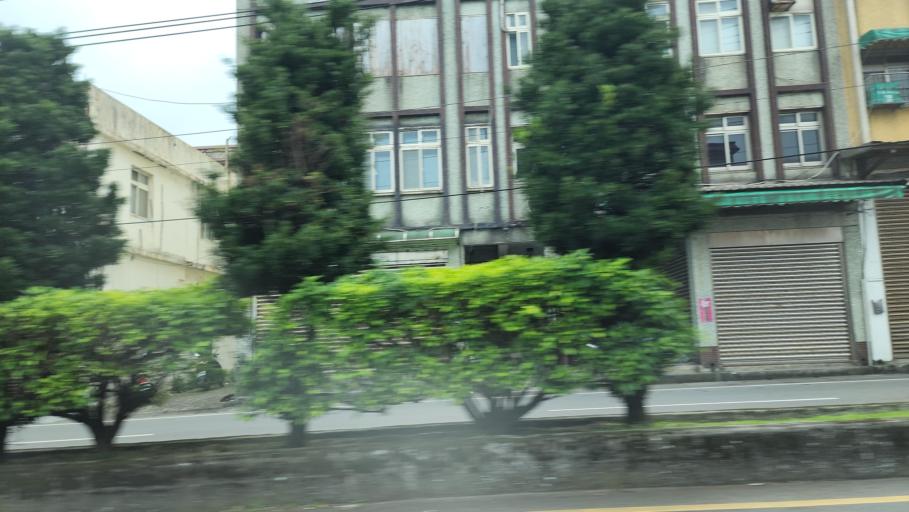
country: TW
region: Taiwan
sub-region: Keelung
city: Keelung
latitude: 25.2127
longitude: 121.6463
